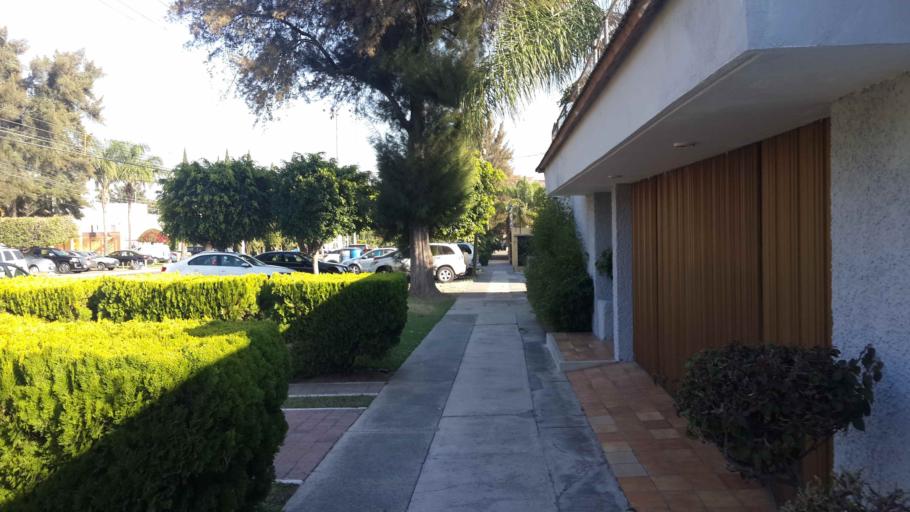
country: MX
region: Jalisco
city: Guadalajara
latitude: 20.6698
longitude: -103.4329
